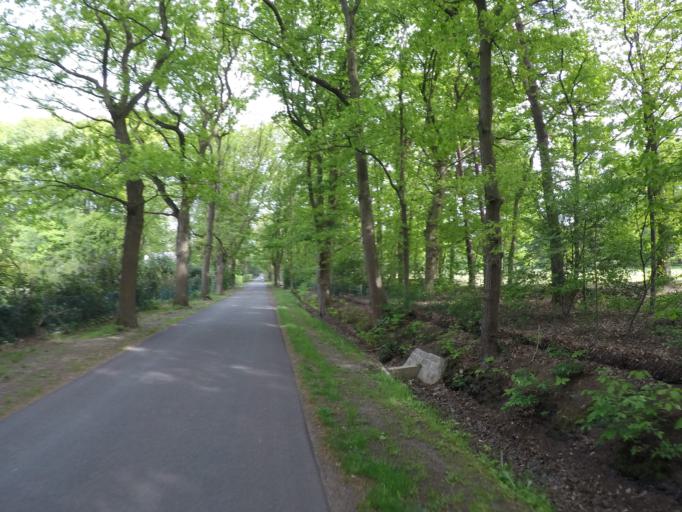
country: BE
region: Flanders
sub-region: Provincie Antwerpen
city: Kalmthout
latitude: 51.3471
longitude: 4.4631
